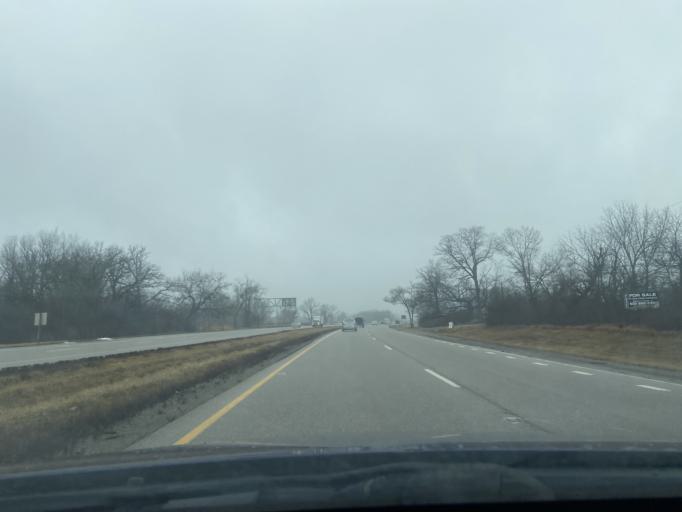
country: US
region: Illinois
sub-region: Lake County
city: Wauconda
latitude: 42.2519
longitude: -88.1467
